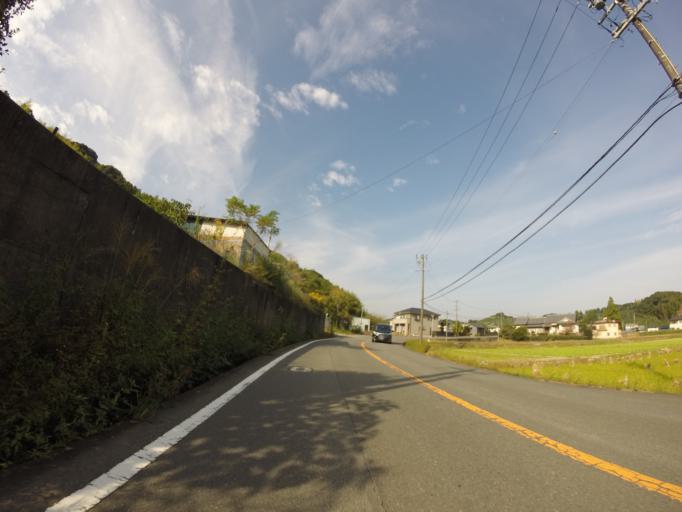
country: JP
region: Shizuoka
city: Shimada
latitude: 34.7521
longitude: 138.1988
